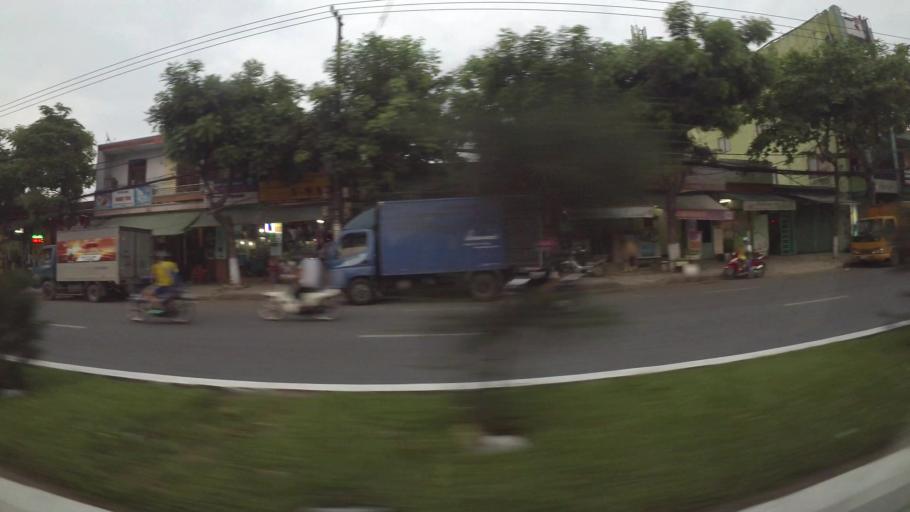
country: VN
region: Da Nang
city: Lien Chieu
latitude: 16.0819
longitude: 108.1463
